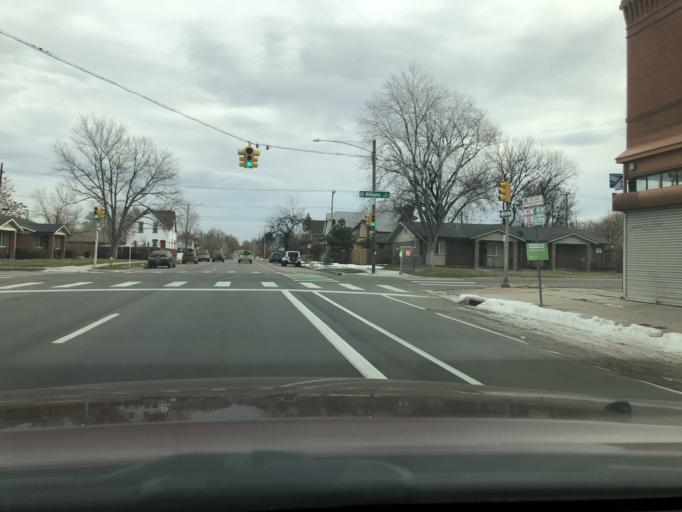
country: US
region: Colorado
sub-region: Denver County
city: Denver
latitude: 39.7607
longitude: -104.9663
